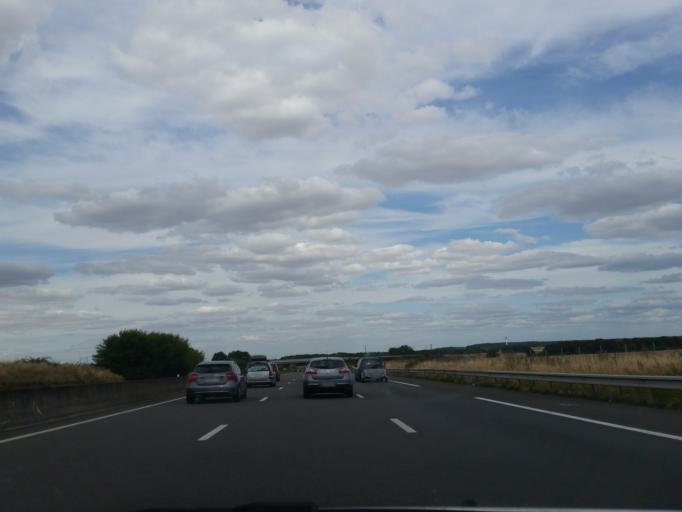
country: FR
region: Centre
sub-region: Departement du Loir-et-Cher
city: Herbault
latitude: 47.5865
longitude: 1.0796
